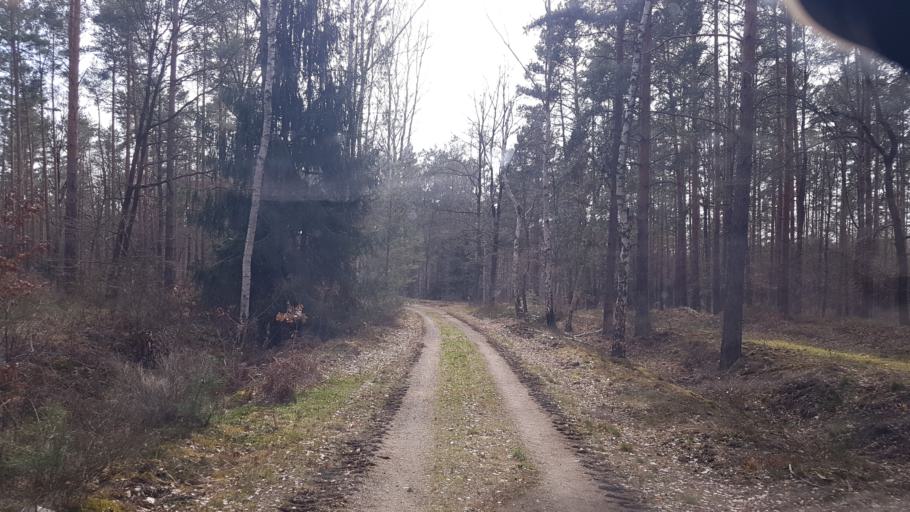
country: DE
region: Brandenburg
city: Lauchhammer
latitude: 51.5376
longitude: 13.7068
